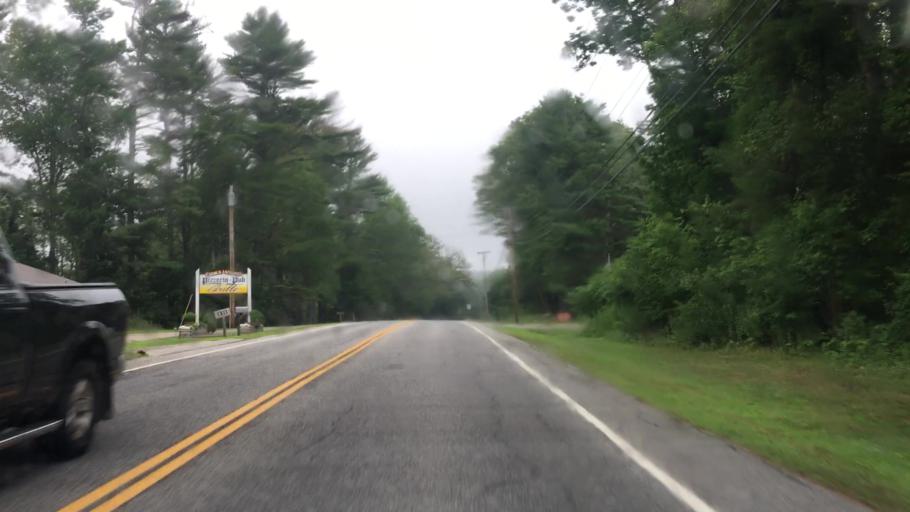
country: US
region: Maine
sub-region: Lincoln County
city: Edgecomb
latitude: 43.9633
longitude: -69.6294
